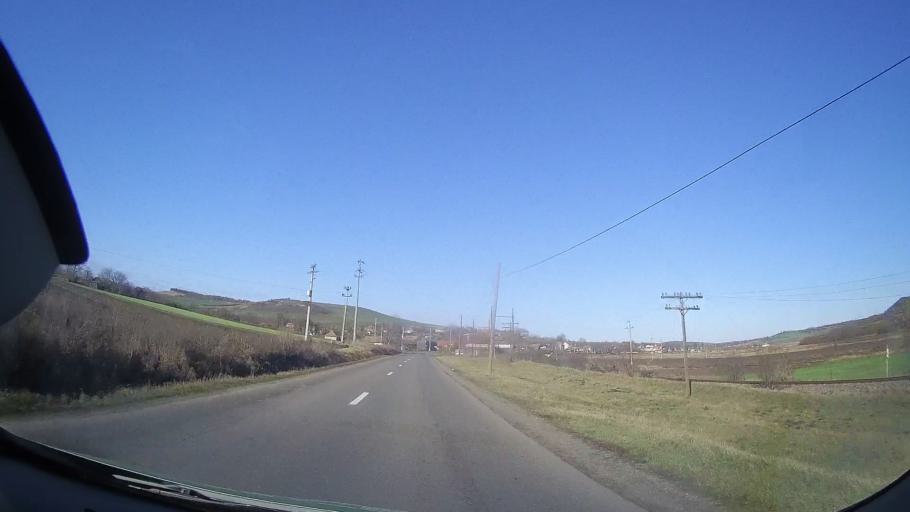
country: RO
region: Mures
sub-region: Comuna Sarmasu
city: Balda
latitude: 46.7215
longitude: 24.1444
